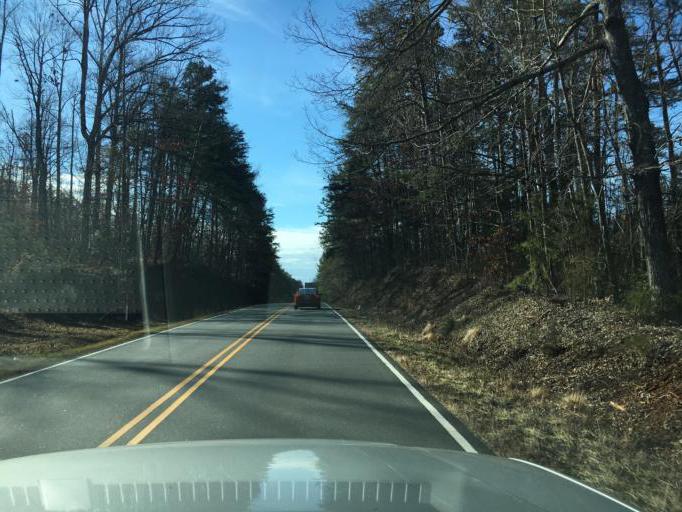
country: US
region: North Carolina
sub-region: Rutherford County
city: Spindale
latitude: 35.4690
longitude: -81.8842
